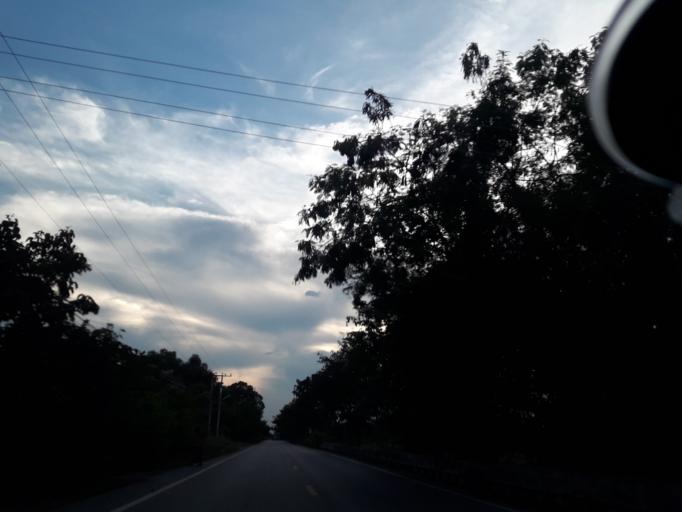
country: TH
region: Sara Buri
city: Nong Khae
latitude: 14.2659
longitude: 100.8708
